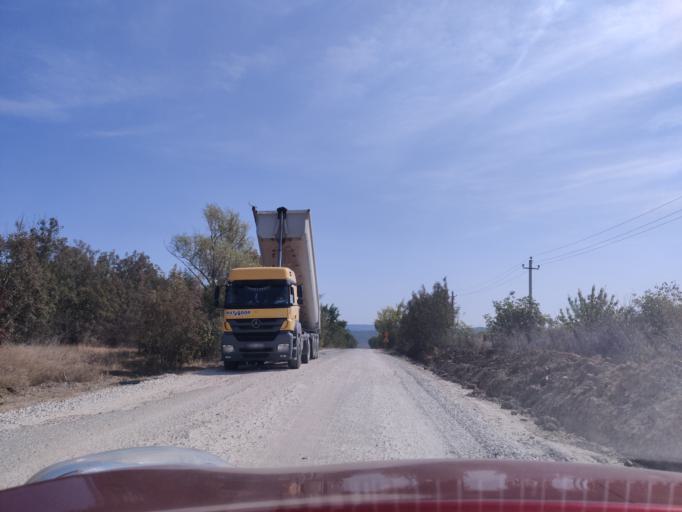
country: MD
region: Ungheni
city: Ungheni
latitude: 47.2643
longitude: 27.9795
